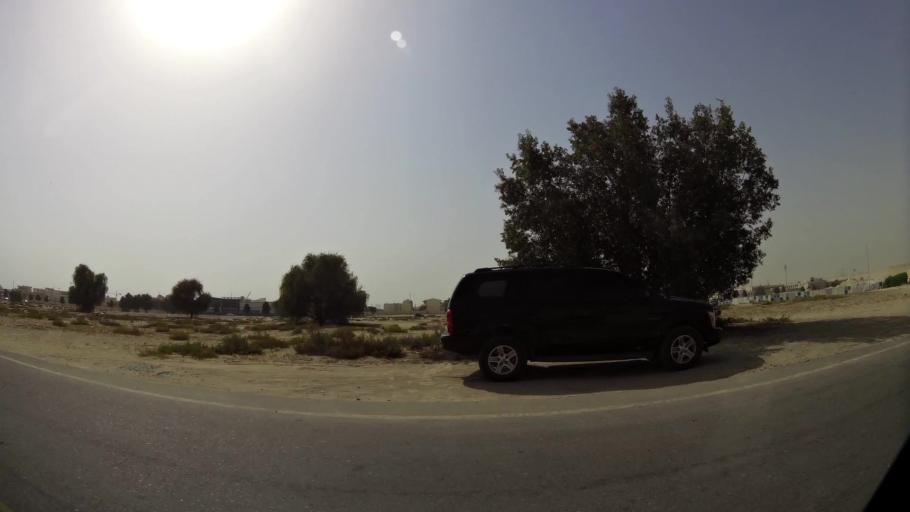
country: AE
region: Ash Shariqah
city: Sharjah
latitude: 25.2640
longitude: 55.4367
